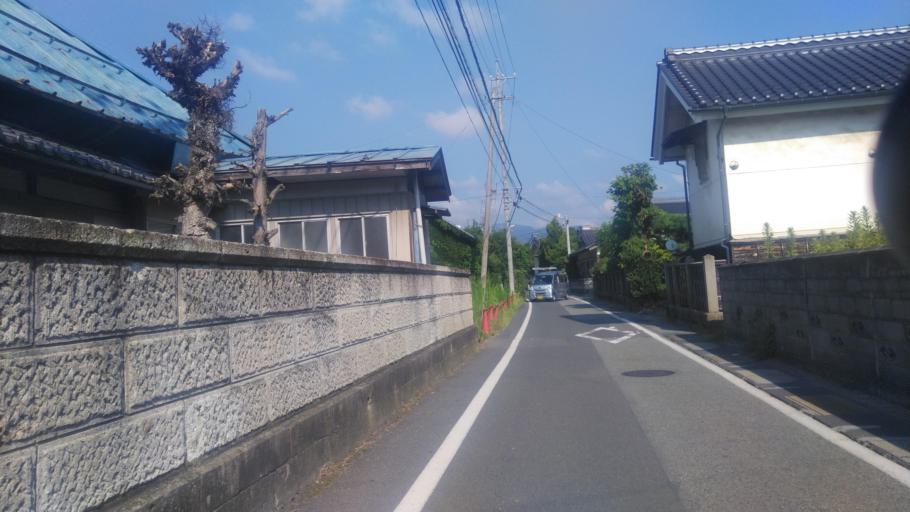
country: JP
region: Nagano
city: Nagano-shi
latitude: 36.6273
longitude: 138.2188
